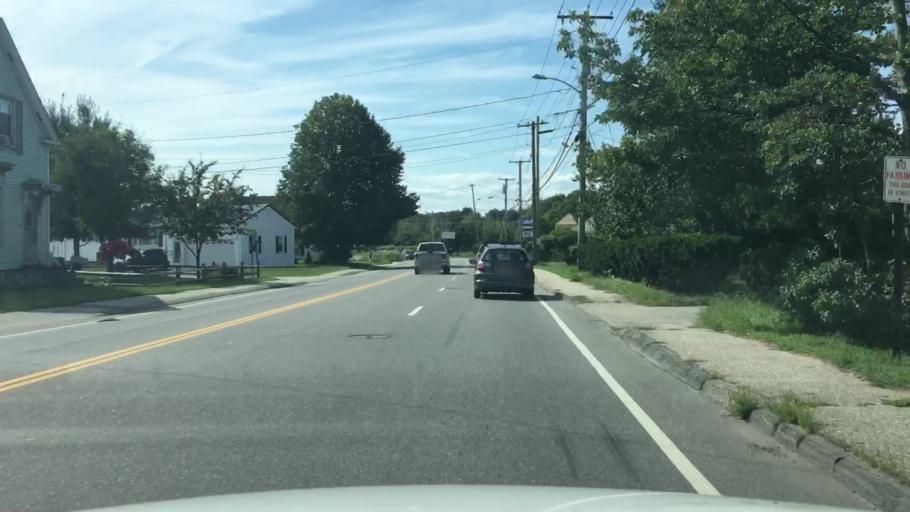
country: US
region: Maine
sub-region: Cumberland County
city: South Portland Gardens
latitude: 43.6302
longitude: -70.2894
